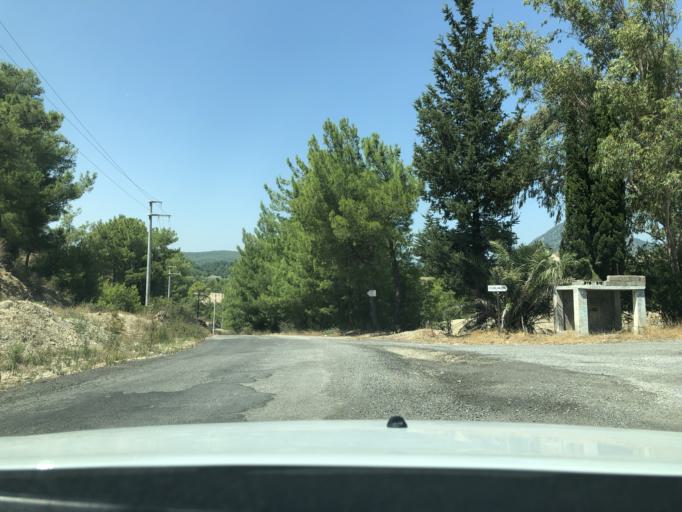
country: TR
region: Antalya
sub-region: Manavgat
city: Kizilagac
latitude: 36.8644
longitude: 31.5607
